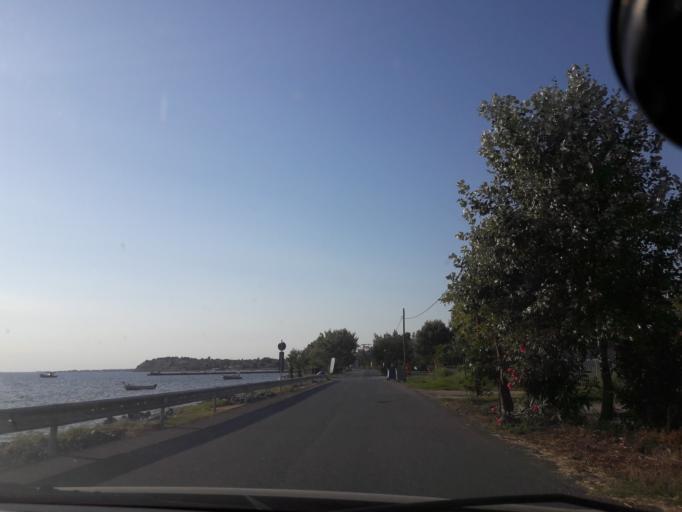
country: GR
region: Central Macedonia
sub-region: Nomos Chalkidikis
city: Nea Kallikrateia
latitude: 40.3410
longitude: 23.0166
